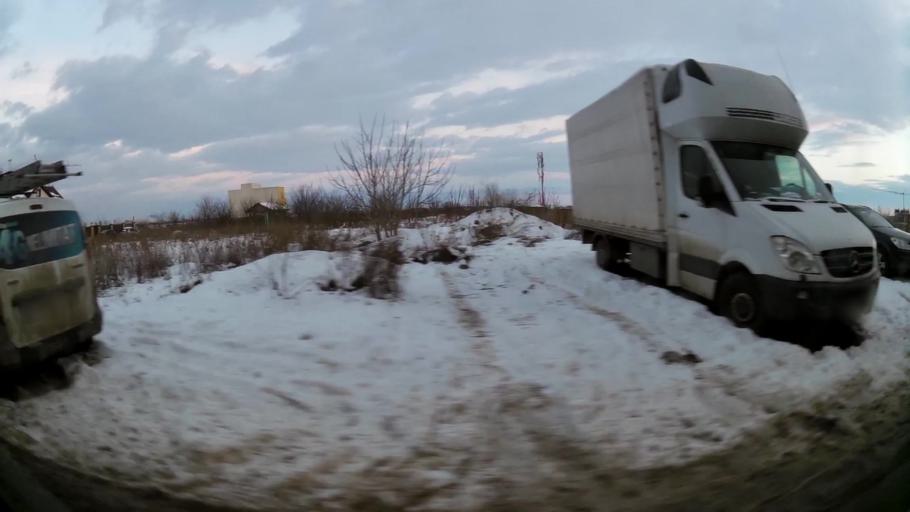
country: RO
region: Ilfov
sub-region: Comuna Popesti-Leordeni
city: Popesti-Leordeni
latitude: 44.3650
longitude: 26.1530
